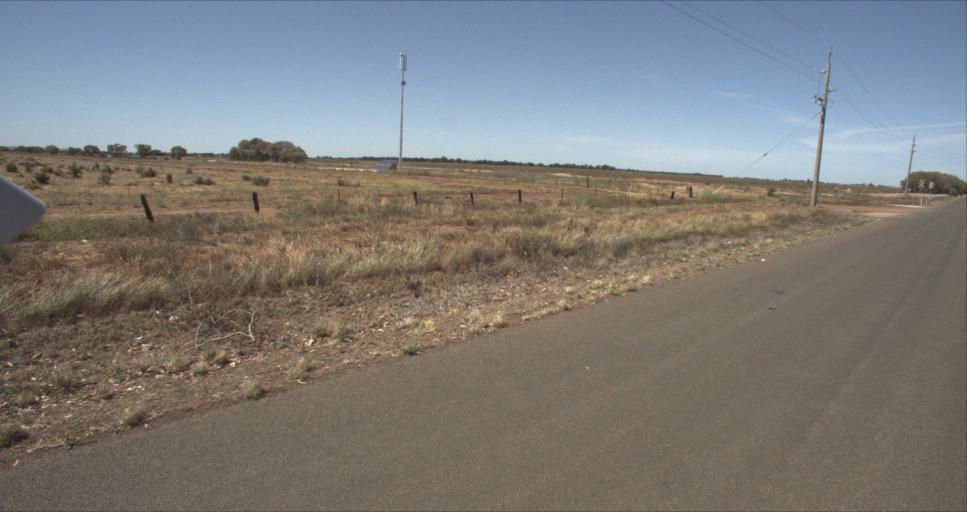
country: AU
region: New South Wales
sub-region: Leeton
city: Leeton
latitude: -34.4729
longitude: 146.2920
